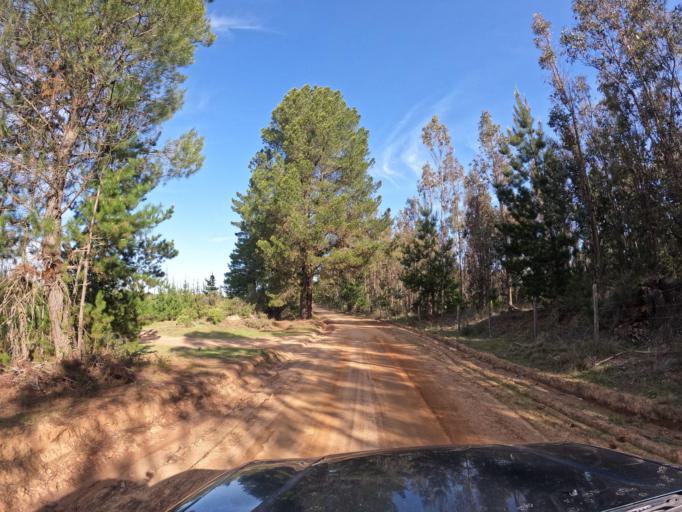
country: CL
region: Biobio
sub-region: Provincia de Biobio
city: La Laja
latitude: -37.1197
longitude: -72.7379
